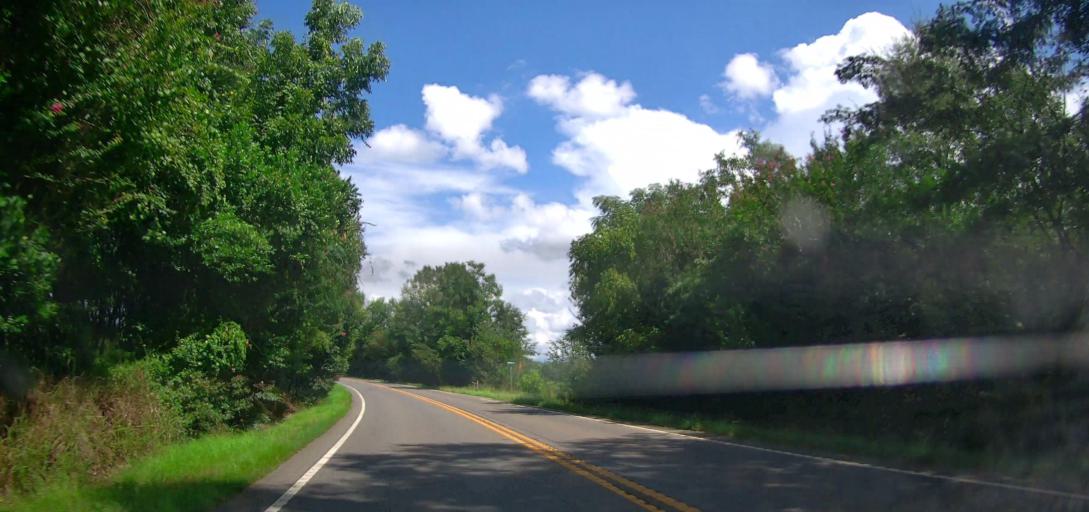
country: US
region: Georgia
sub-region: Macon County
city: Marshallville
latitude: 32.4485
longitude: -83.9720
